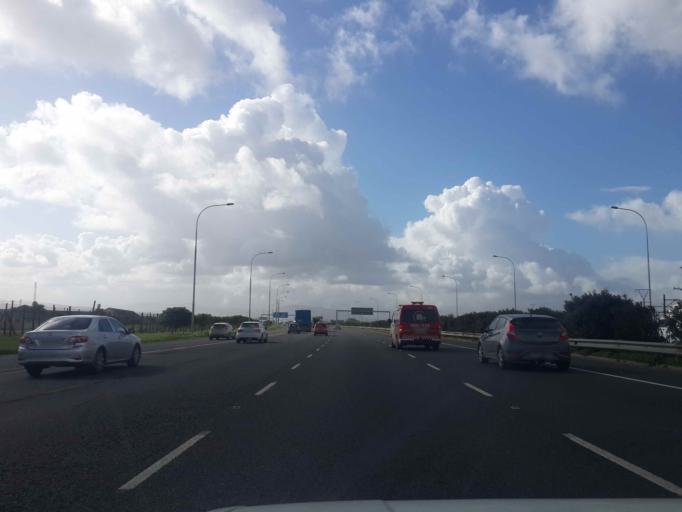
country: ZA
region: Western Cape
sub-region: City of Cape Town
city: Rosebank
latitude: -33.9161
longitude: 18.4889
